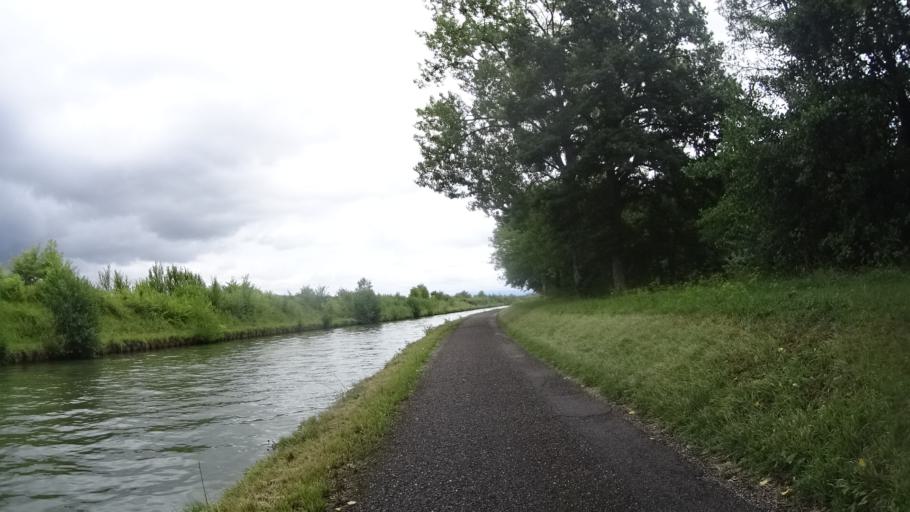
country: FR
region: Lorraine
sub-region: Departement de la Moselle
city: Lorquin
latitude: 48.7034
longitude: 6.9034
